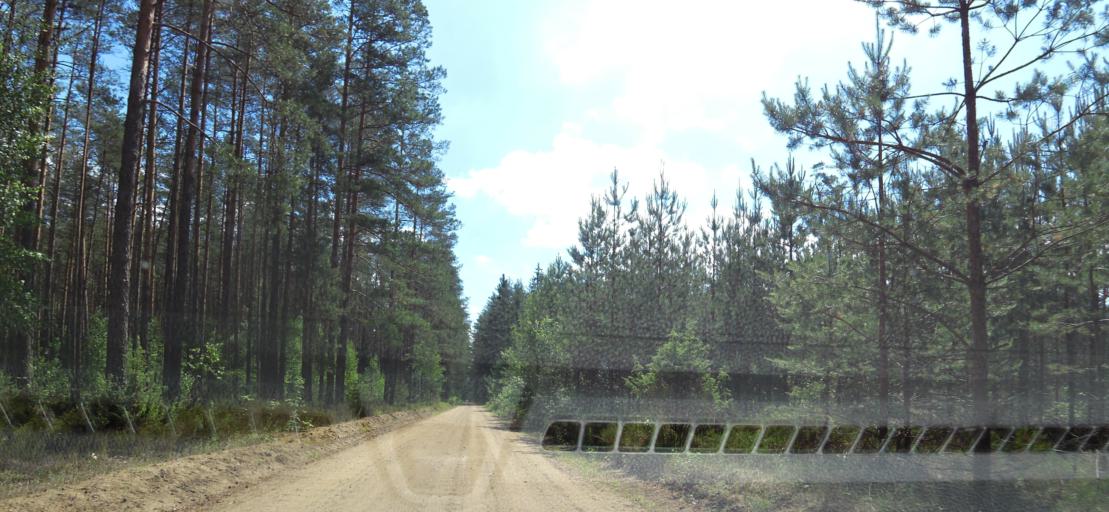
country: LT
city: Nemencine
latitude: 54.8328
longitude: 25.4314
